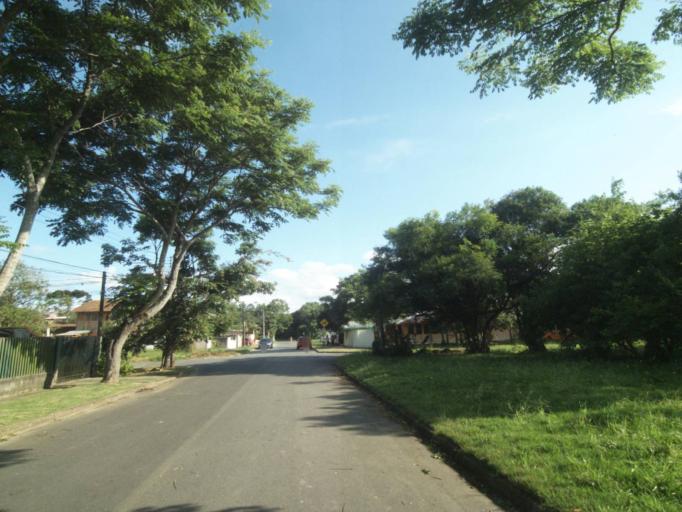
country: BR
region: Parana
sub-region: Curitiba
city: Curitiba
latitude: -25.3905
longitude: -49.3041
